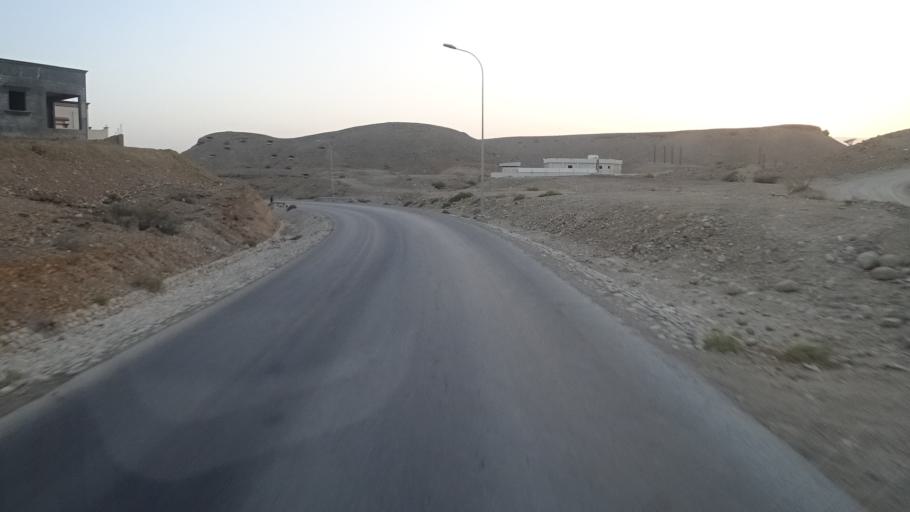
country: OM
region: Ash Sharqiyah
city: Sur
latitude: 22.5438
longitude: 59.4967
